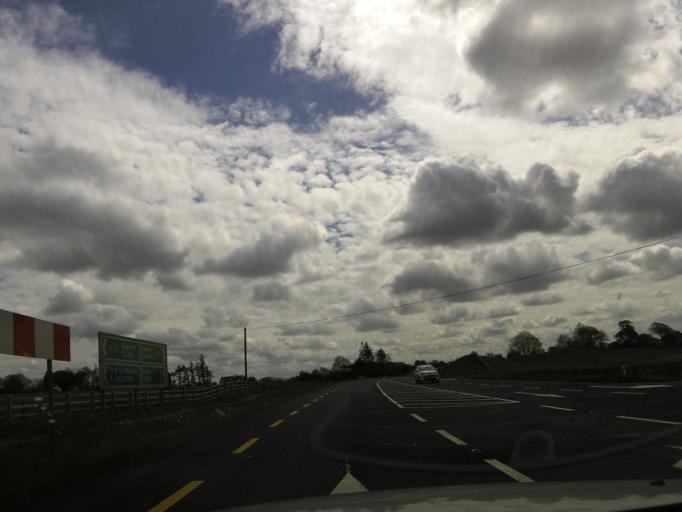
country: IE
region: Connaught
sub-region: County Galway
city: Tuam
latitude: 53.5705
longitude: -8.8405
